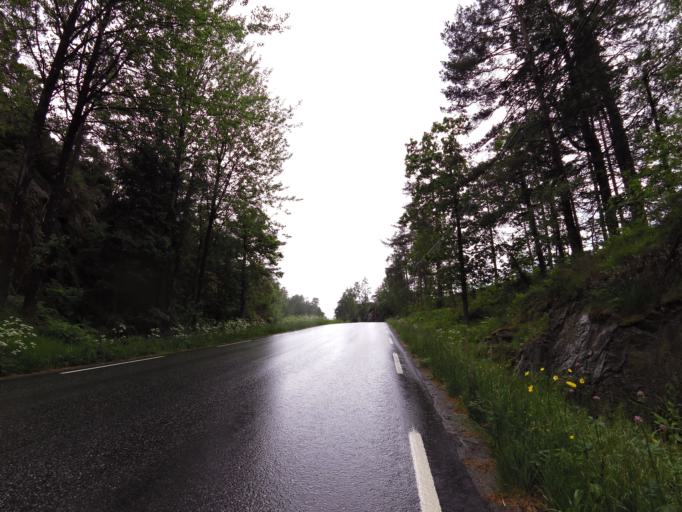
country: NO
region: Vest-Agder
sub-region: Mandal
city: Mandal
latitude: 58.0224
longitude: 7.5166
